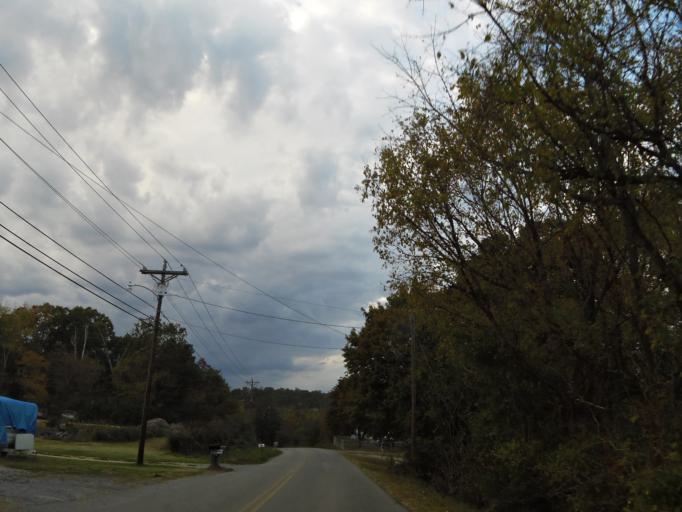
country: US
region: Tennessee
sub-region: Blount County
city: Louisville
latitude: 35.7760
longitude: -84.0493
